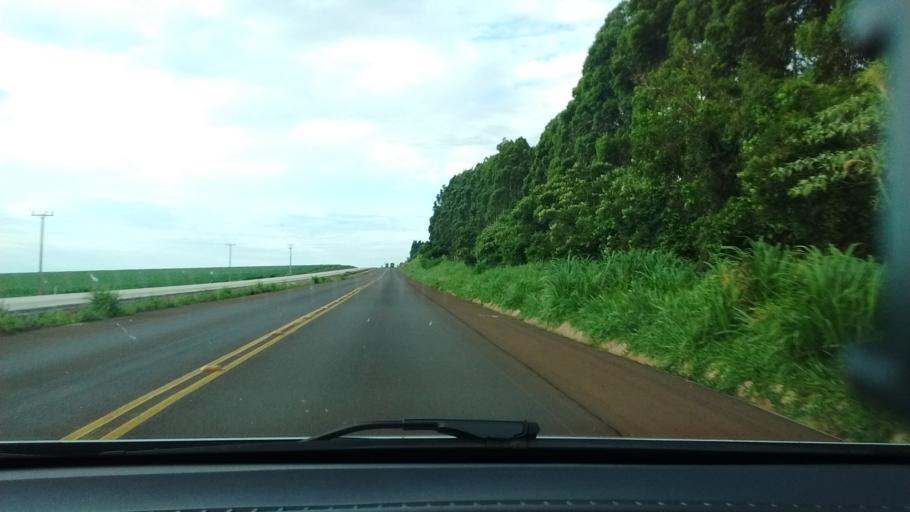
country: BR
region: Parana
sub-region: Cascavel
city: Cascavel
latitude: -25.0517
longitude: -53.5588
